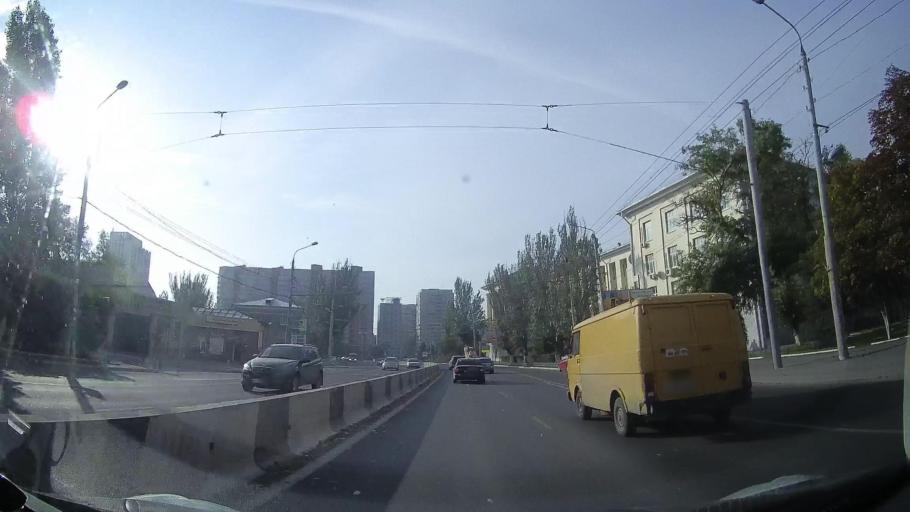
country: RU
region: Rostov
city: Rostov-na-Donu
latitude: 47.2382
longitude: 39.7135
